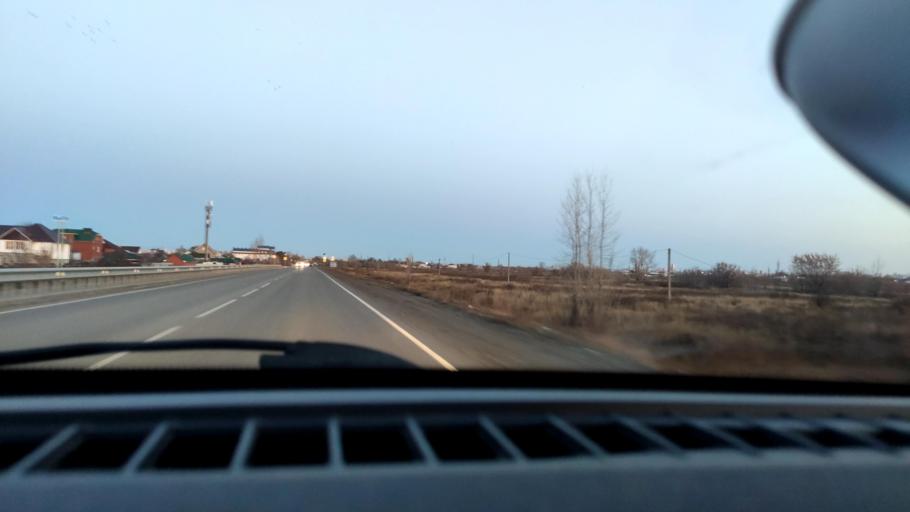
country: RU
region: Samara
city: Samara
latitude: 53.1205
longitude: 50.1196
